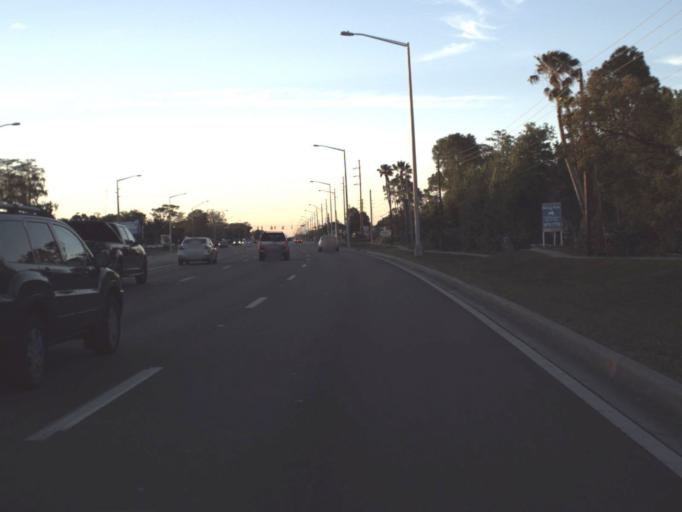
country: US
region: Florida
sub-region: Seminole County
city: Goldenrod
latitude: 28.6085
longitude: -81.3078
